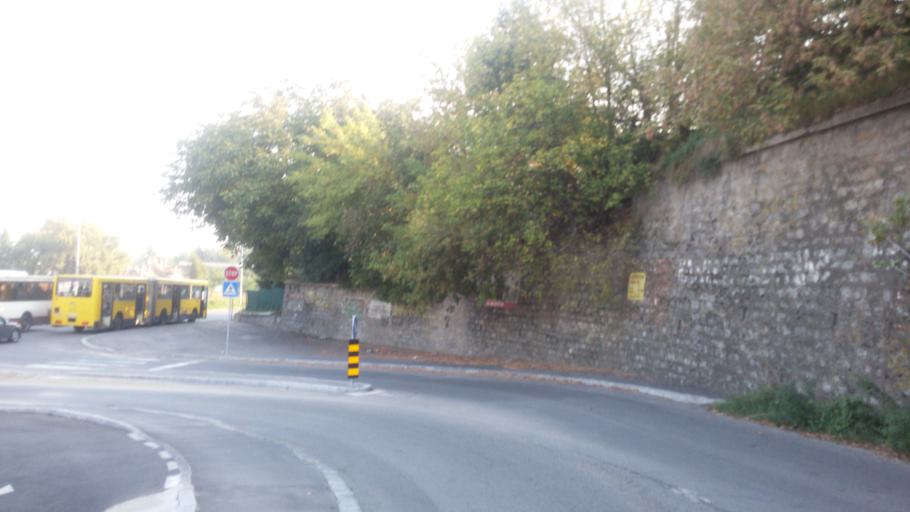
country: RS
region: Central Serbia
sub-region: Belgrade
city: Cukarica
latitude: 44.7490
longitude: 20.4003
